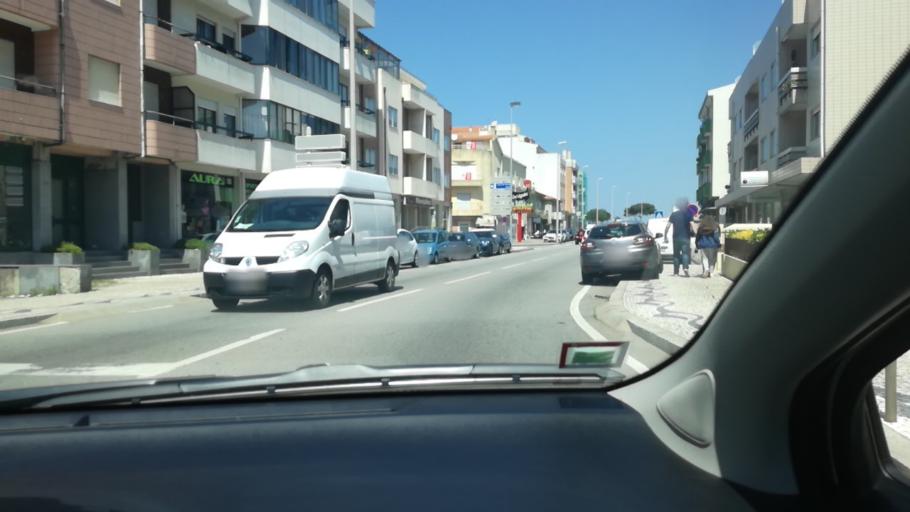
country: PT
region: Porto
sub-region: Povoa de Varzim
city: Povoa de Varzim
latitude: 41.3887
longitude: -8.7659
